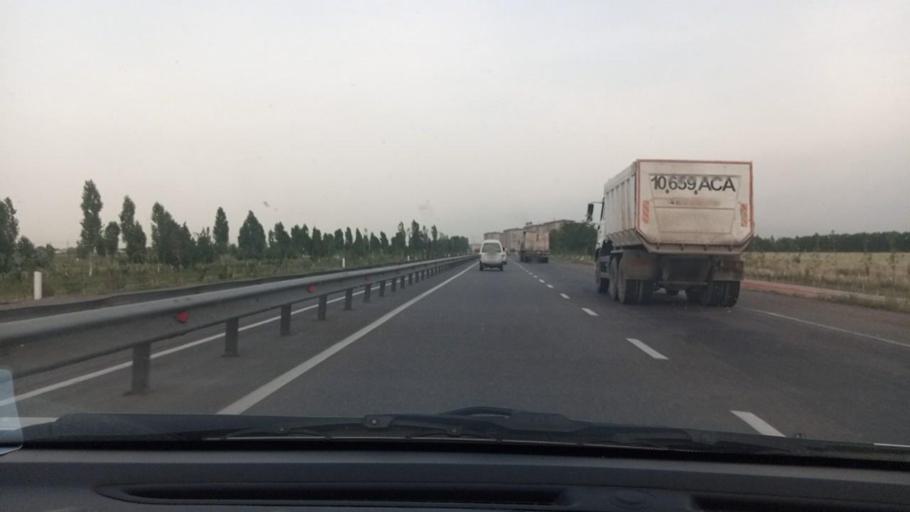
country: UZ
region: Toshkent
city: Ohangaron
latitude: 40.9175
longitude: 69.6029
